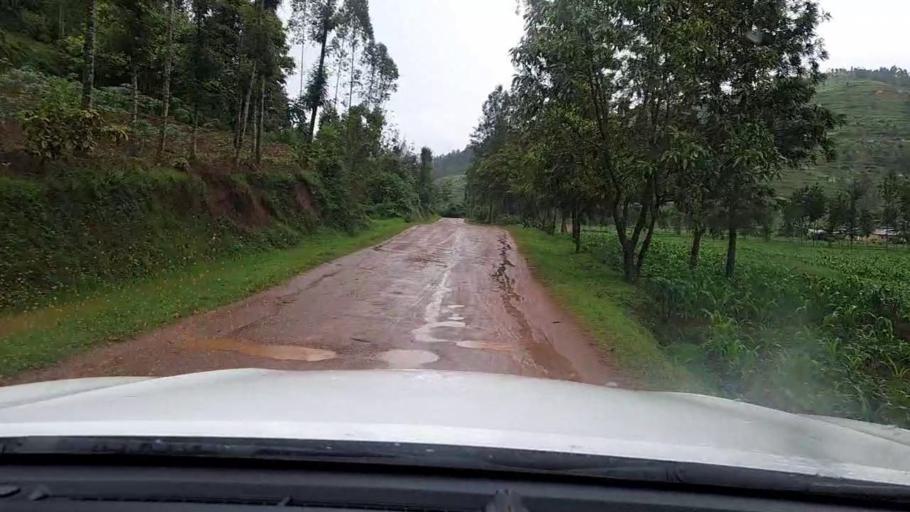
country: RW
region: Northern Province
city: Byumba
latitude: -1.7348
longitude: 29.9406
